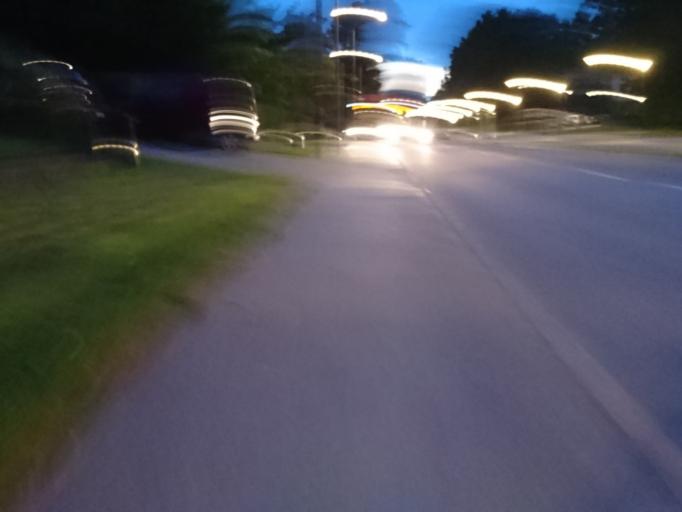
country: SE
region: Stockholm
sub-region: Huddinge Kommun
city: Segeltorp
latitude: 59.2803
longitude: 17.9683
